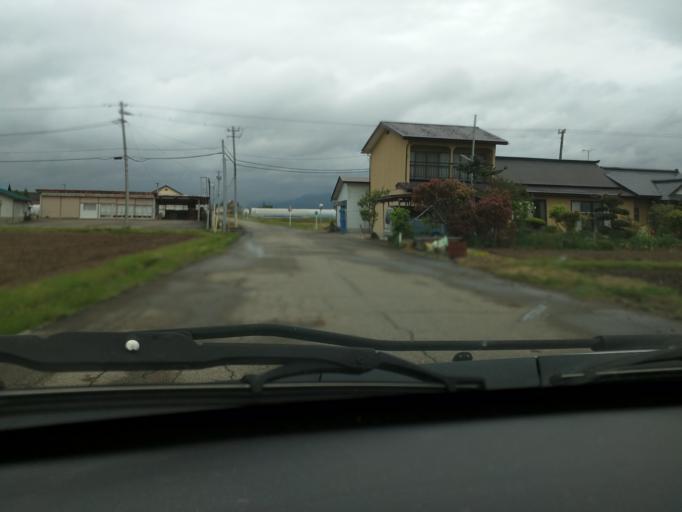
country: JP
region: Fukushima
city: Kitakata
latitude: 37.6082
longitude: 139.8690
